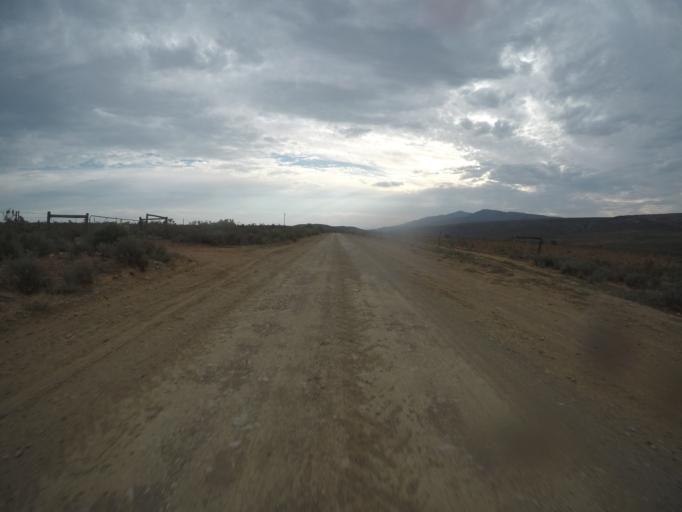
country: ZA
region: Eastern Cape
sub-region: Cacadu District Municipality
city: Willowmore
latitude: -33.4924
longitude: 23.5771
